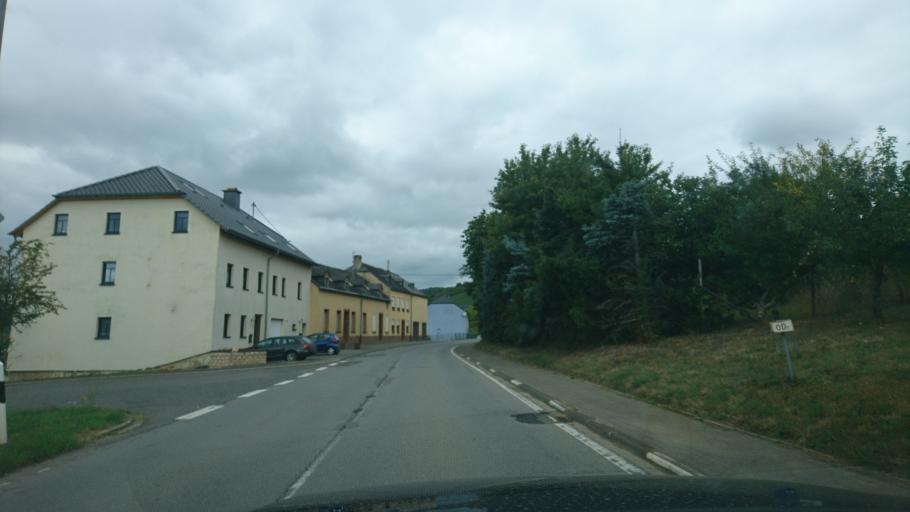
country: DE
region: Rheinland-Pfalz
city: Pellingen
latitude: 49.6865
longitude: 6.6402
